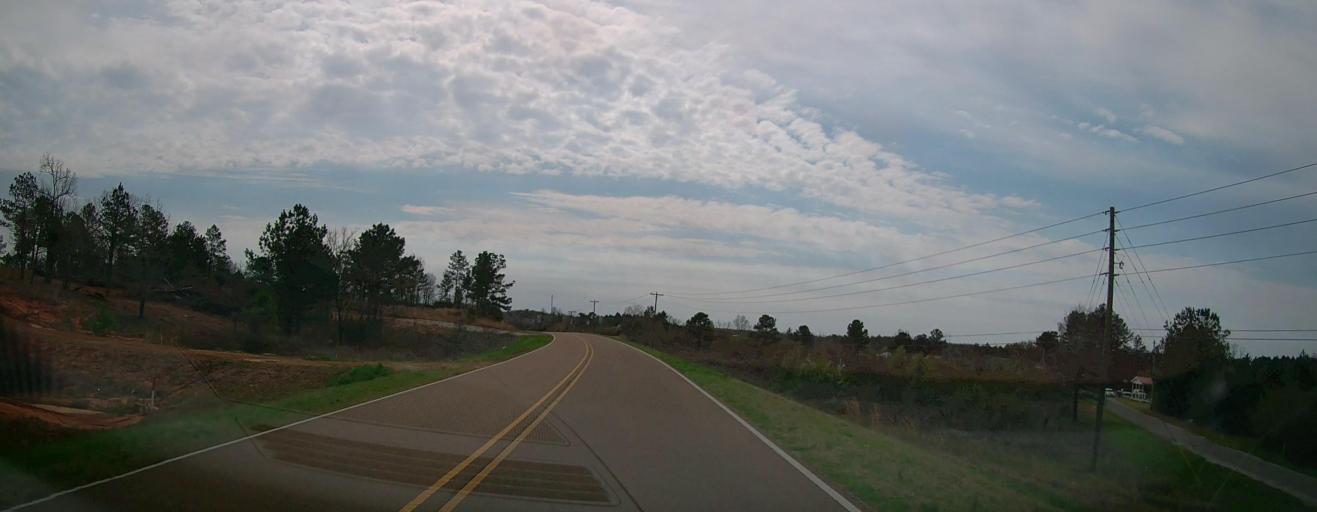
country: US
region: Mississippi
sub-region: Marshall County
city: Holly Springs
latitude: 34.7520
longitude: -89.4298
